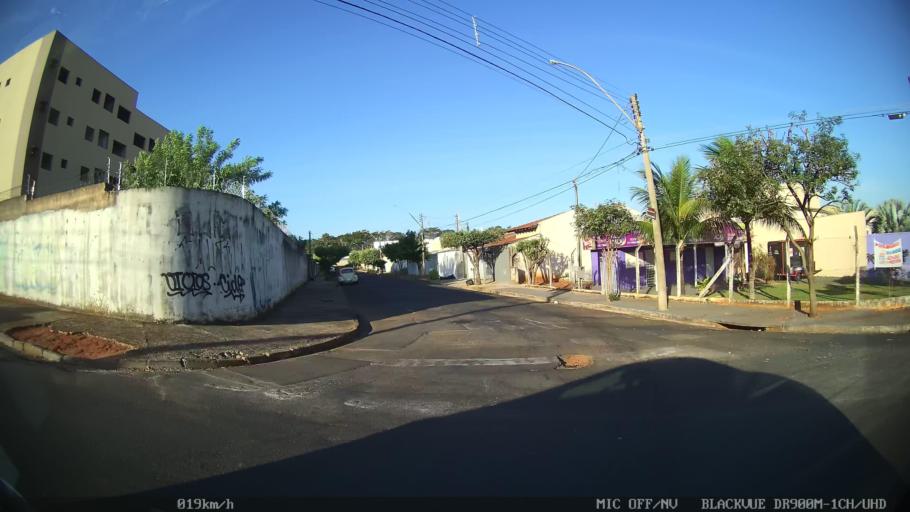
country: BR
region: Sao Paulo
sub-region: Sao Jose Do Rio Preto
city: Sao Jose do Rio Preto
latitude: -20.7963
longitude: -49.3576
